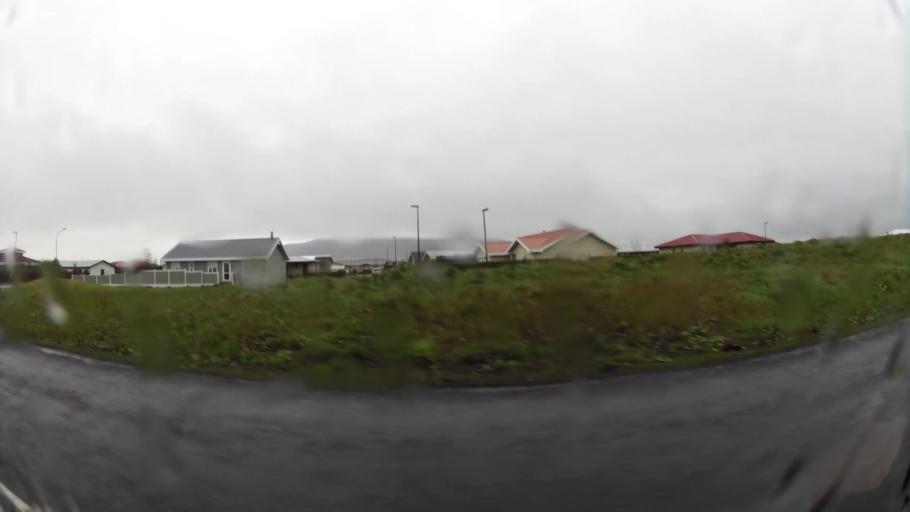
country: IS
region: South
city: Selfoss
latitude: 63.9231
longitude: -20.9905
